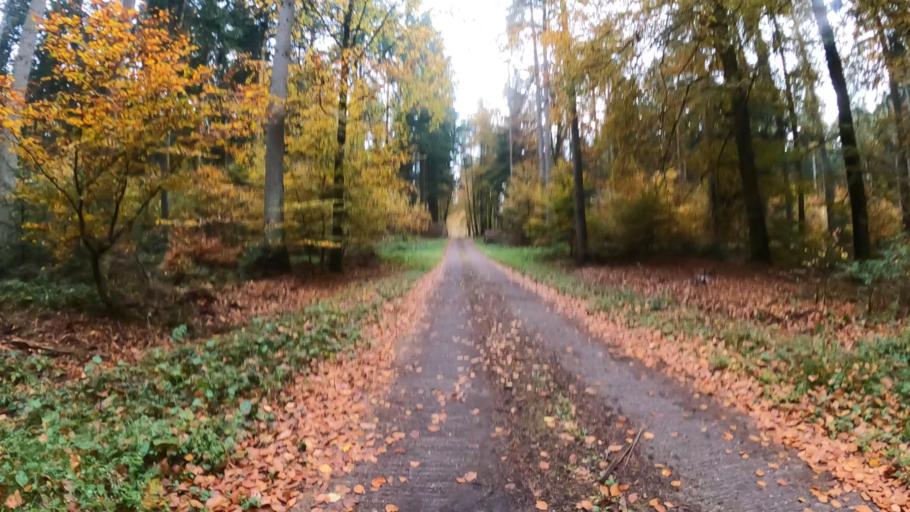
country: DE
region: Lower Saxony
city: Buchholz in der Nordheide
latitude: 53.3669
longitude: 9.8242
